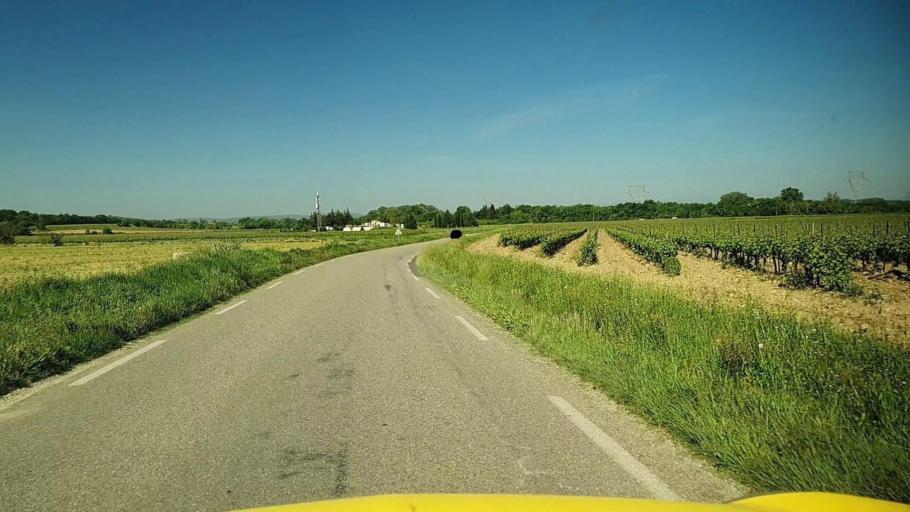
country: FR
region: Languedoc-Roussillon
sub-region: Departement du Gard
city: Blauzac
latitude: 43.9422
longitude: 4.3213
